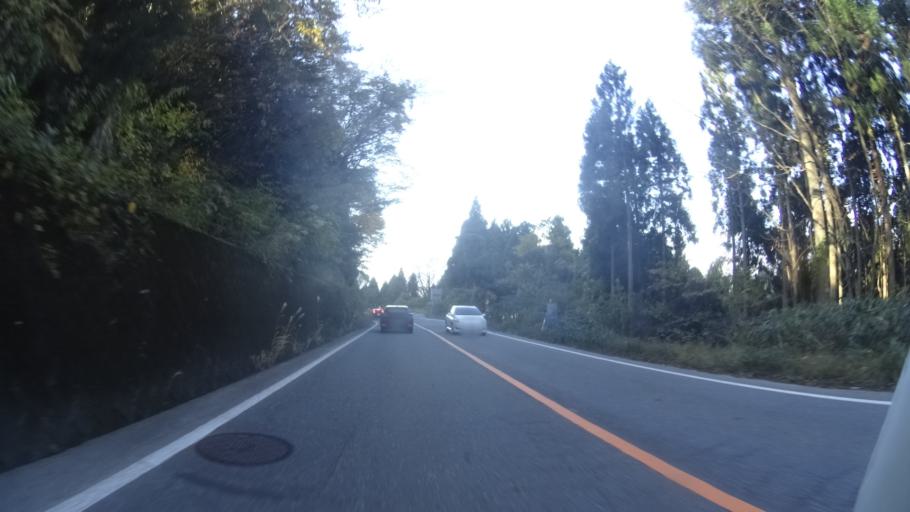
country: JP
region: Fukui
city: Ono
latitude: 35.9704
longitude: 136.5683
